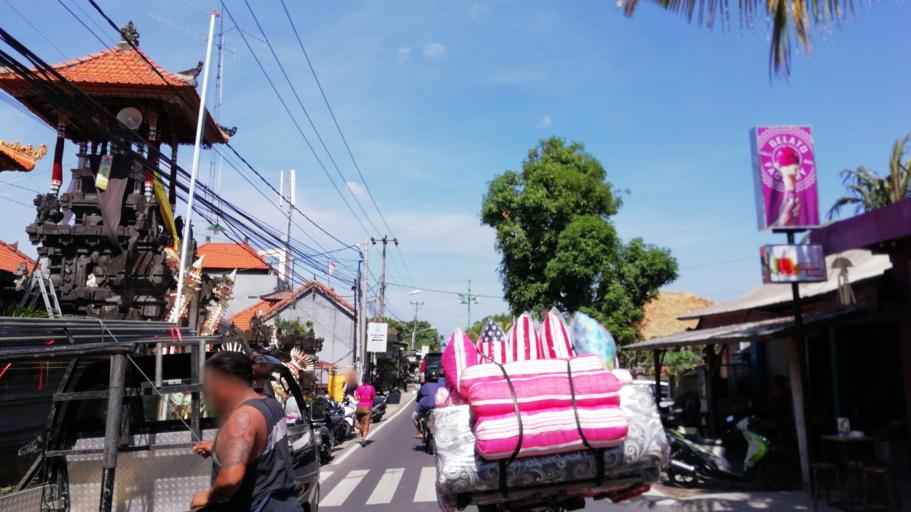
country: ID
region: Bali
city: Banjar Kerobokan
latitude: -8.6483
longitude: 115.1388
